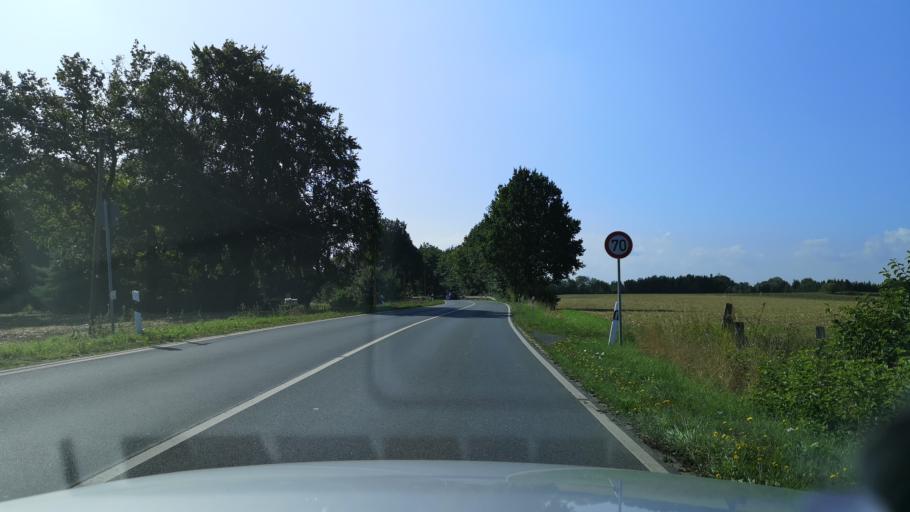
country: DE
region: North Rhine-Westphalia
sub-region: Regierungsbezirk Arnsberg
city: Frondenberg
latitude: 51.4985
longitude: 7.7716
